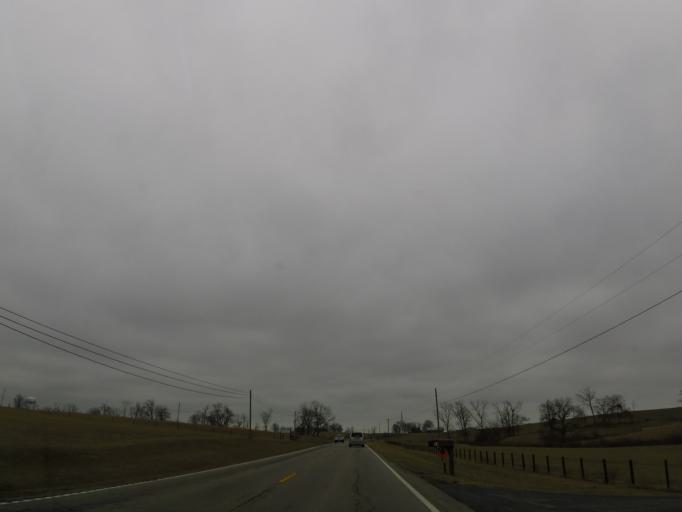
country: US
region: Kentucky
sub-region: Henry County
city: New Castle
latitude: 38.4734
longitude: -85.1709
